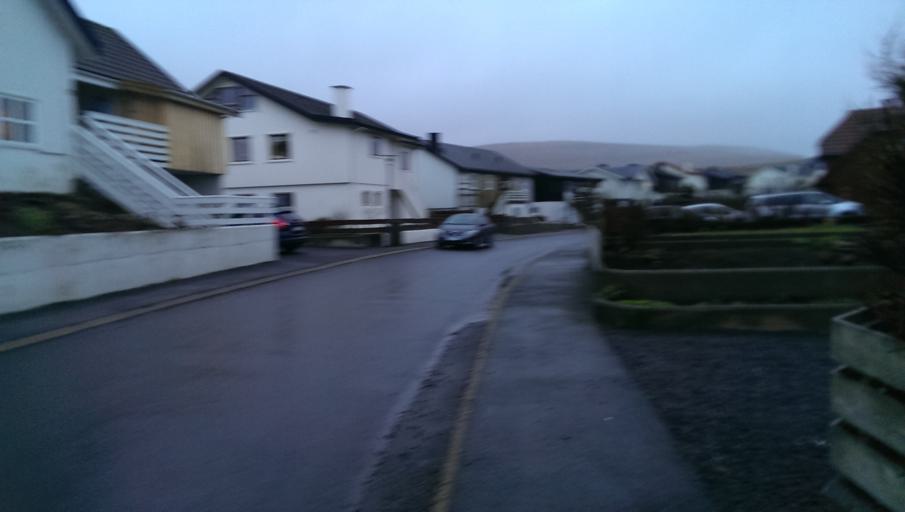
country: FO
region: Streymoy
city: Hoyvik
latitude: 62.0318
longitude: -6.7865
